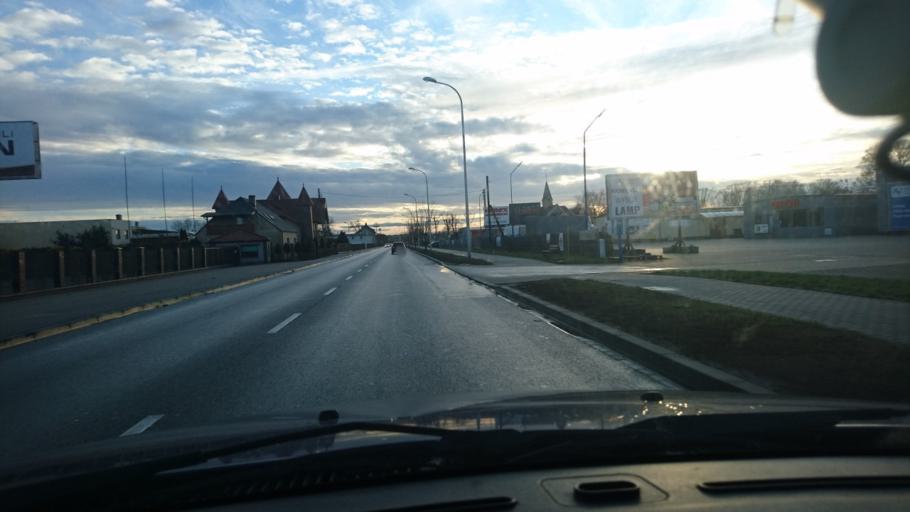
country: PL
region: Greater Poland Voivodeship
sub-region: Powiat kepinski
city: Kepno
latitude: 51.2939
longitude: 17.9958
